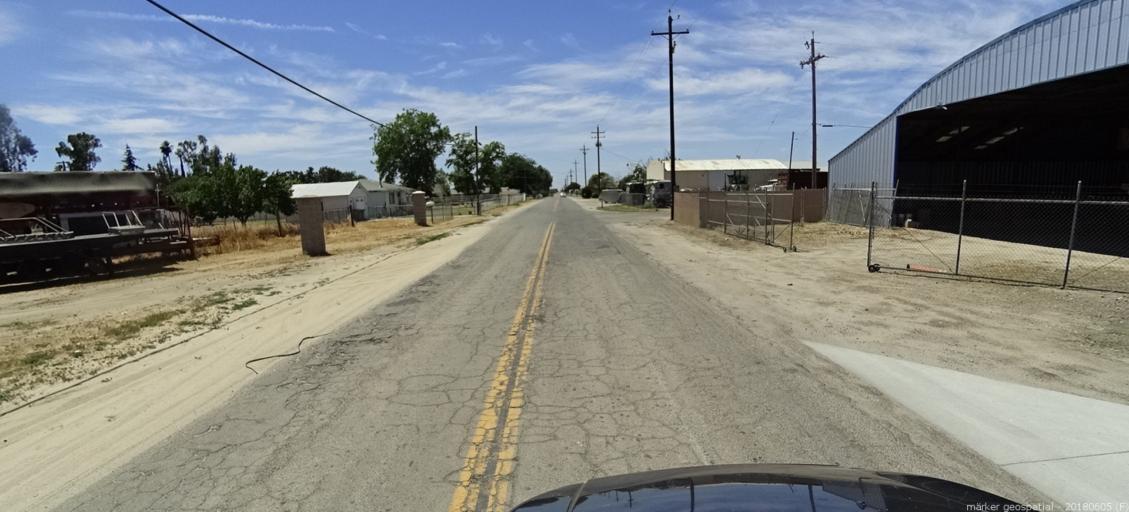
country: US
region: California
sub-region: Madera County
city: Chowchilla
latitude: 37.0908
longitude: -120.2923
